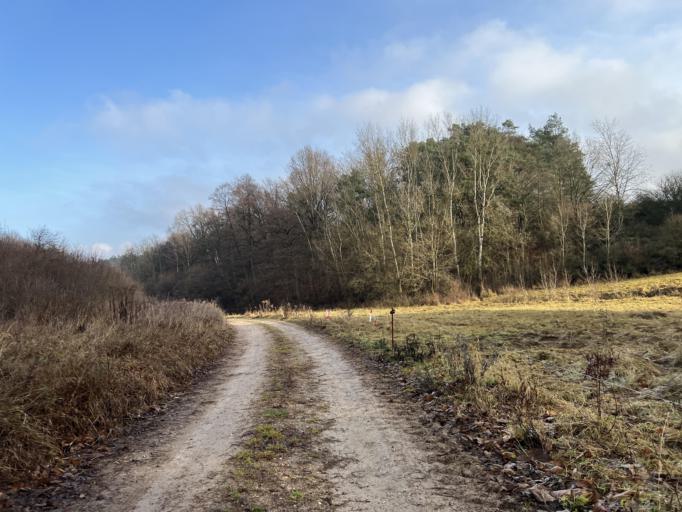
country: DE
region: Brandenburg
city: Eberswalde
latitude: 52.8319
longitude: 13.8703
